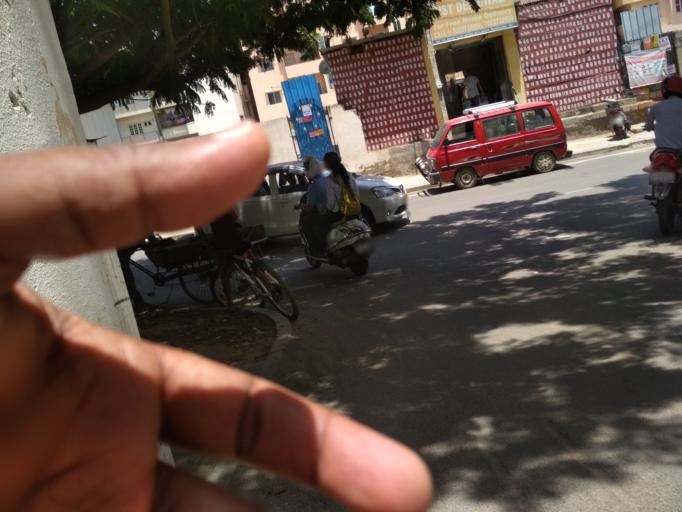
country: IN
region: Karnataka
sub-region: Bangalore Urban
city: Bangalore
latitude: 12.9290
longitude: 77.6711
